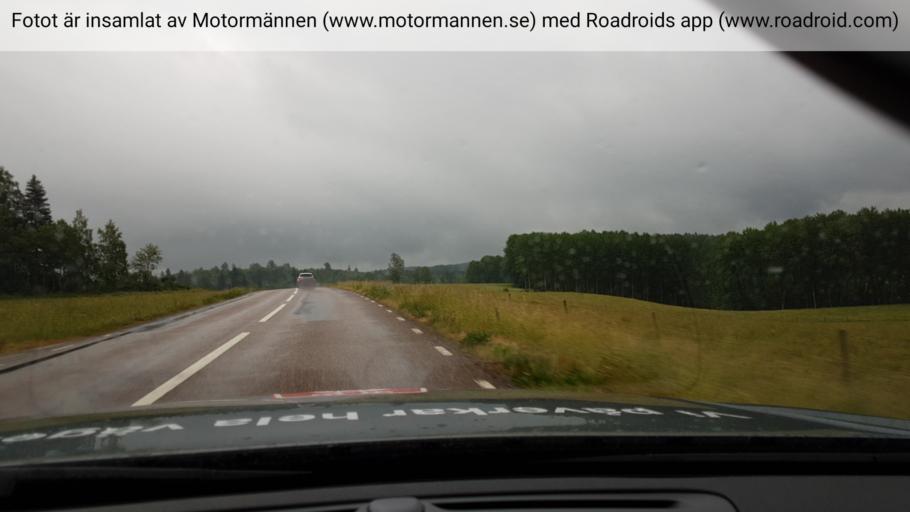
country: SE
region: Dalarna
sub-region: Avesta Kommun
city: Avesta
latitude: 59.9969
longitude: 16.0939
